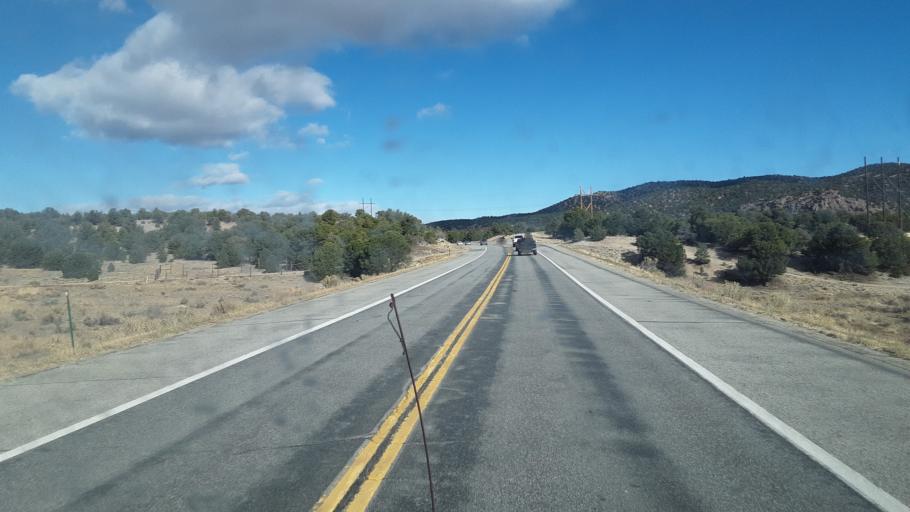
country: US
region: Colorado
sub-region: Chaffee County
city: Salida
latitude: 38.6232
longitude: -106.0778
